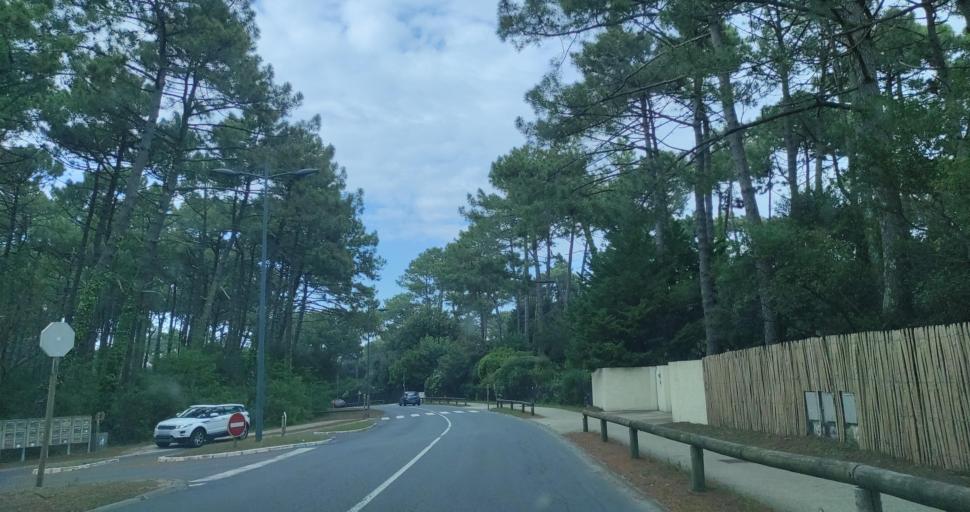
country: FR
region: Aquitaine
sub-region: Departement de la Gironde
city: Arcachon
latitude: 44.6847
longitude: -1.2378
